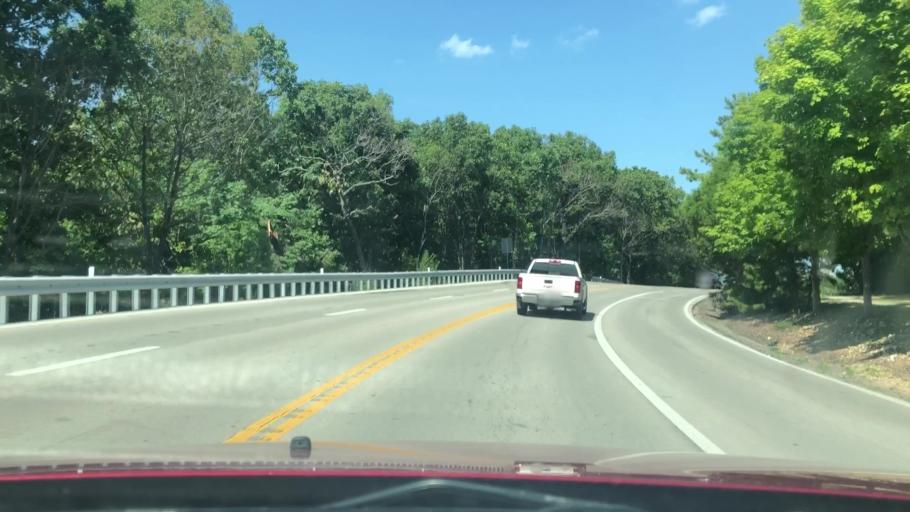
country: US
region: Missouri
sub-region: Stone County
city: Kimberling City
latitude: 36.6744
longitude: -93.3286
